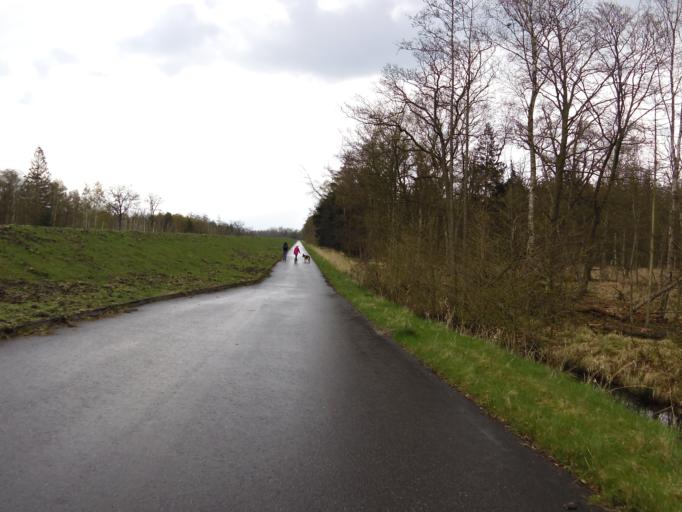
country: DE
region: Mecklenburg-Vorpommern
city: Barth
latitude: 54.4347
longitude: 12.7908
